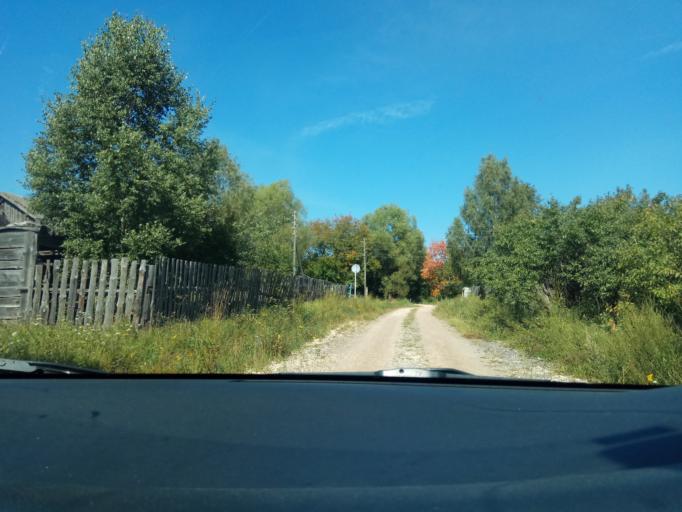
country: RU
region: Vladimir
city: Dobryatino
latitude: 55.7681
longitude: 41.4131
